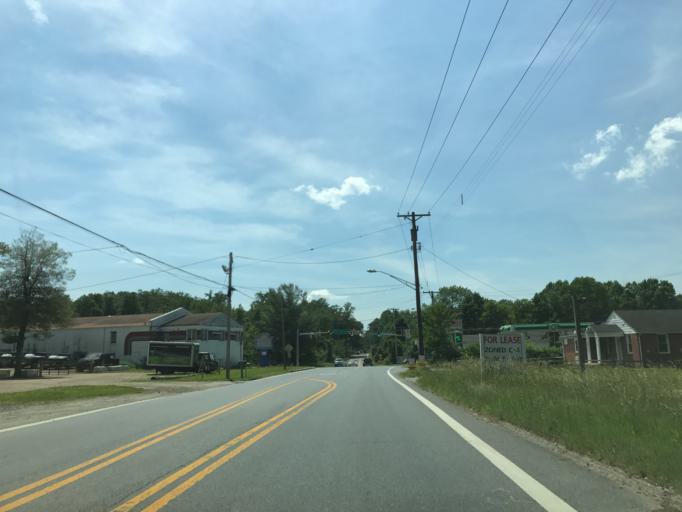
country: US
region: Maryland
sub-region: Anne Arundel County
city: Riva
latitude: 38.9880
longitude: -76.5841
